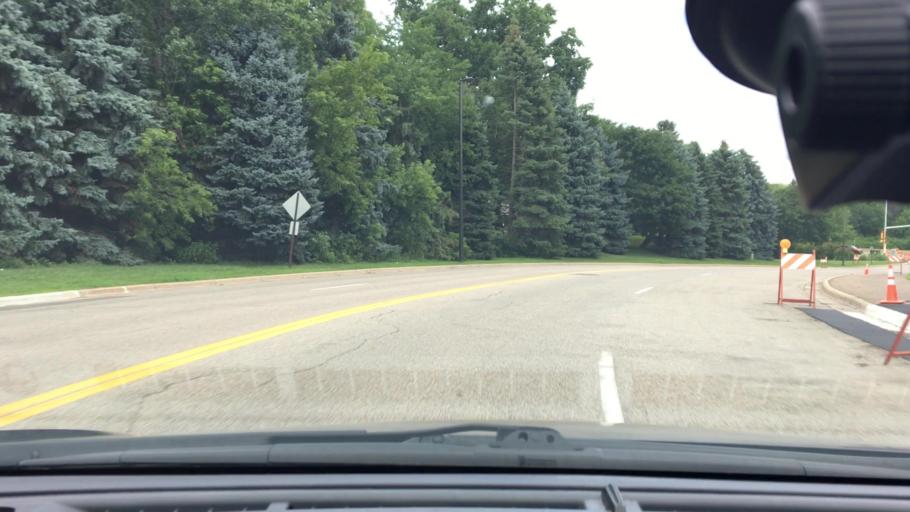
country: US
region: Minnesota
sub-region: Hennepin County
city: Plymouth
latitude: 45.0324
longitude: -93.4487
